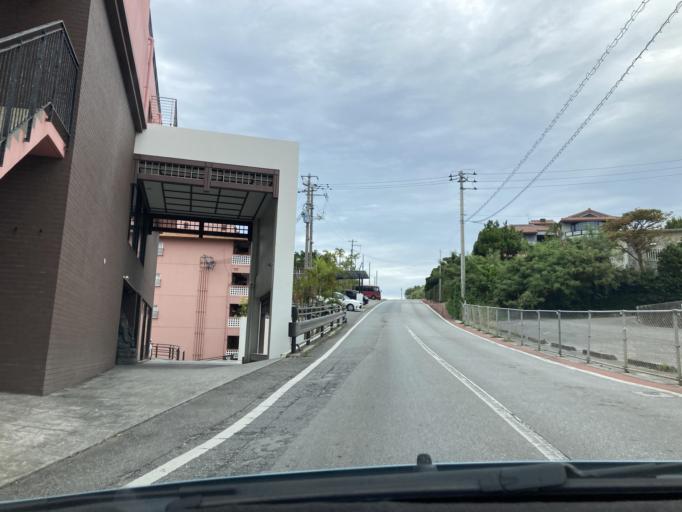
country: JP
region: Okinawa
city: Okinawa
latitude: 26.3854
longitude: 127.7394
